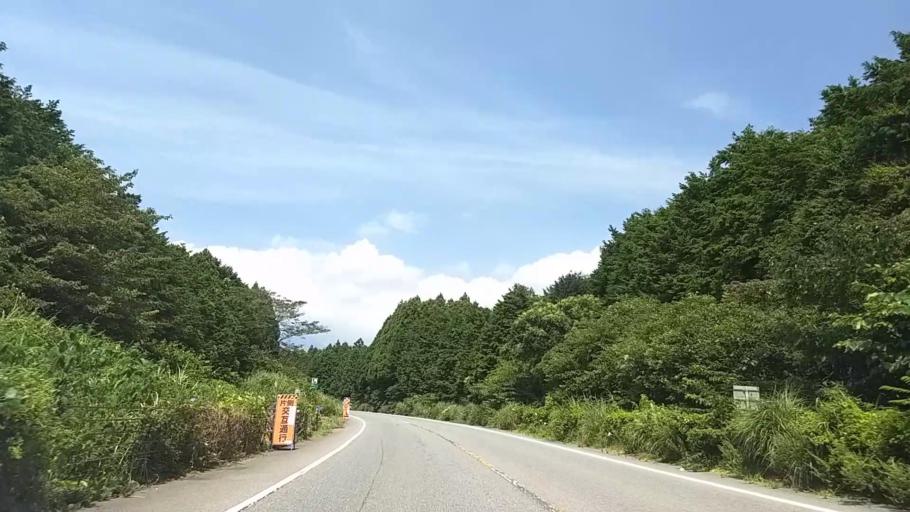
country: JP
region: Shizuoka
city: Fujinomiya
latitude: 35.3233
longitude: 138.5903
